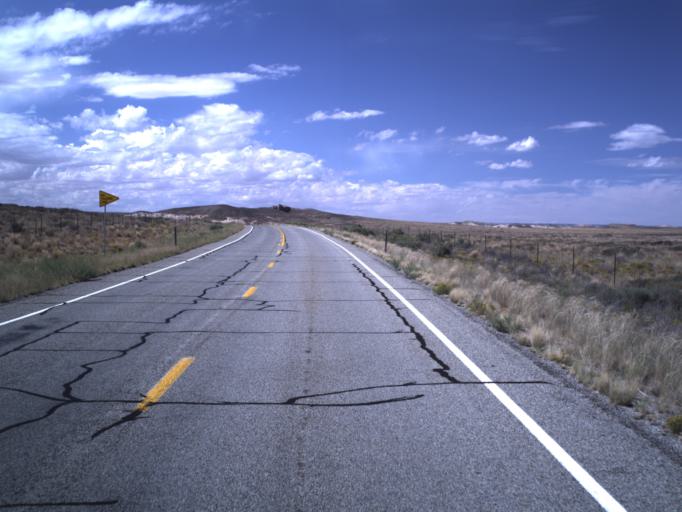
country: US
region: Utah
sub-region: San Juan County
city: Blanding
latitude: 37.2971
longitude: -109.4774
